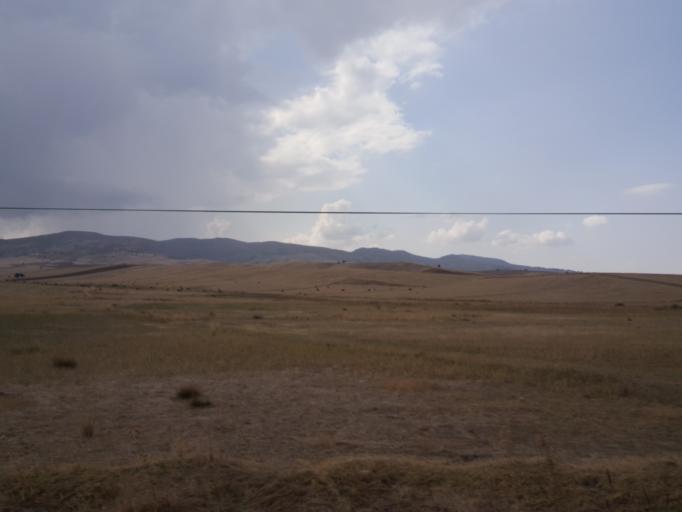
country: TR
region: Corum
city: Bogazkale
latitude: 40.1004
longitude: 34.5531
